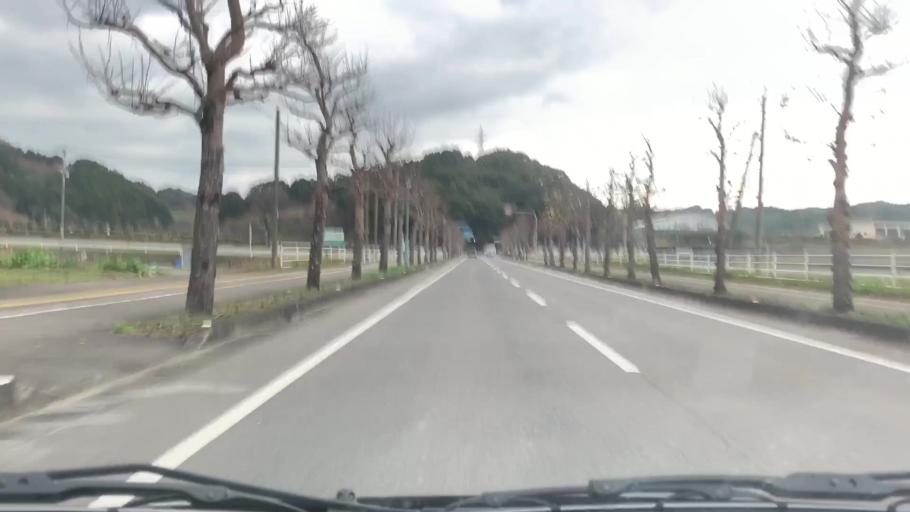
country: JP
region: Saga Prefecture
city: Ureshinomachi-shimojuku
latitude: 33.1056
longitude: 129.9851
